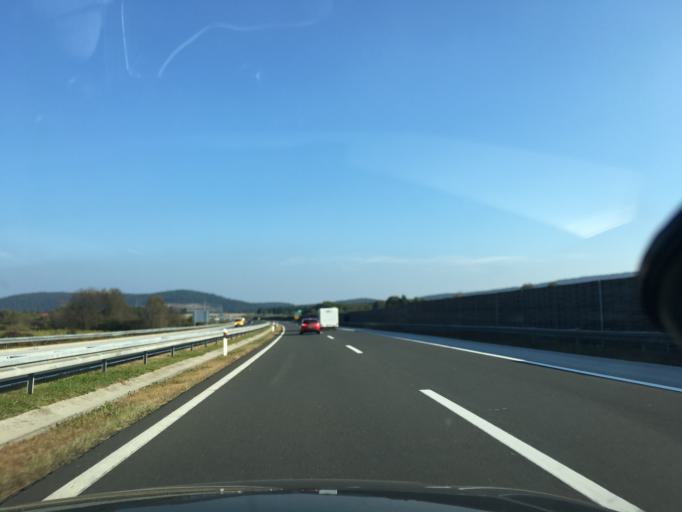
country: HR
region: Karlovacka
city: Ostarije
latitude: 45.2307
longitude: 15.2669
